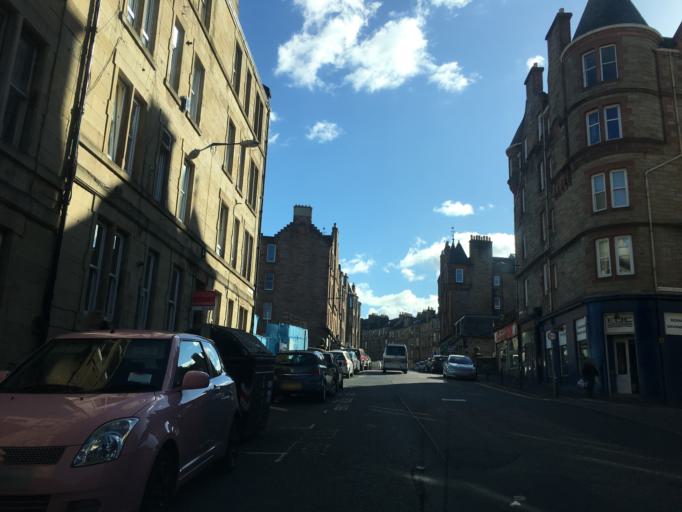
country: GB
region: Scotland
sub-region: Edinburgh
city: Edinburgh
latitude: 55.9394
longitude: -3.2188
